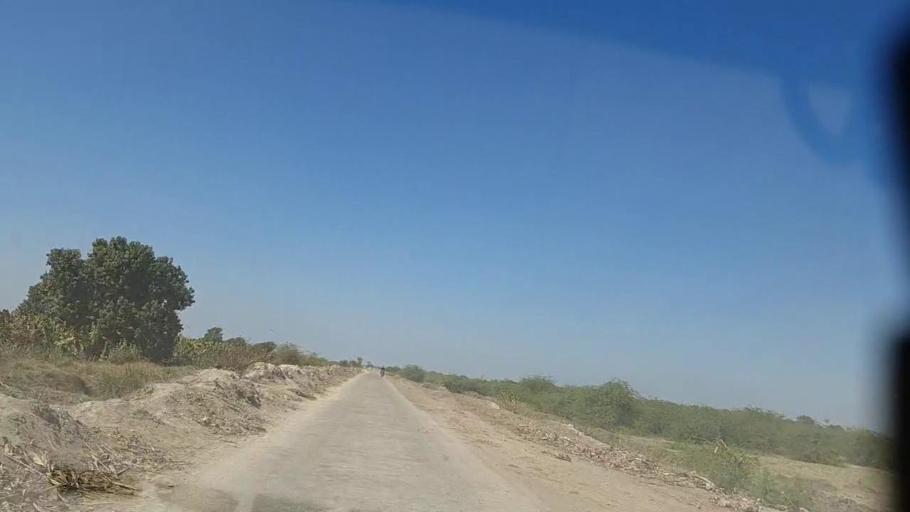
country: PK
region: Sindh
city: Mirwah Gorchani
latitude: 25.2198
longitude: 69.0264
